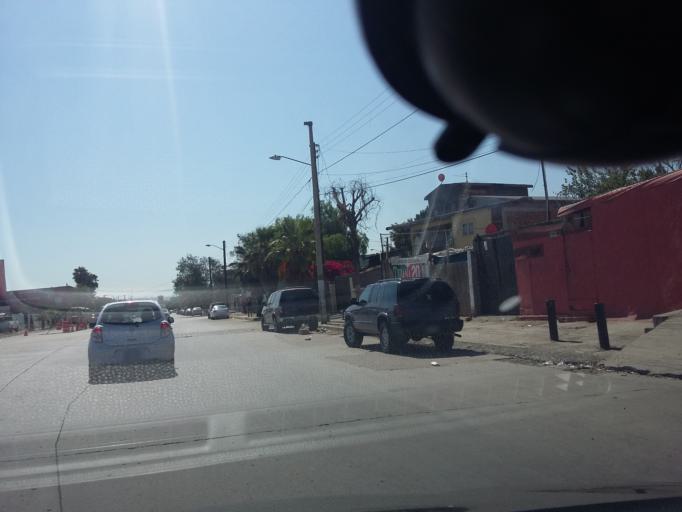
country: MX
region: Baja California
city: Tijuana
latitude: 32.5412
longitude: -117.0401
